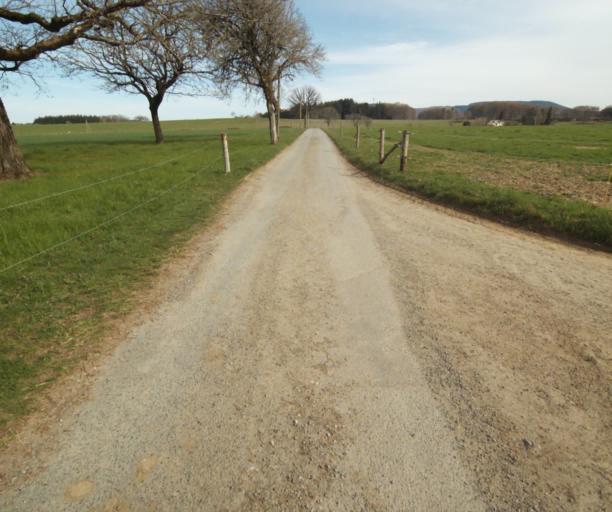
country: FR
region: Limousin
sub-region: Departement de la Correze
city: Correze
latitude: 45.4157
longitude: 1.8203
